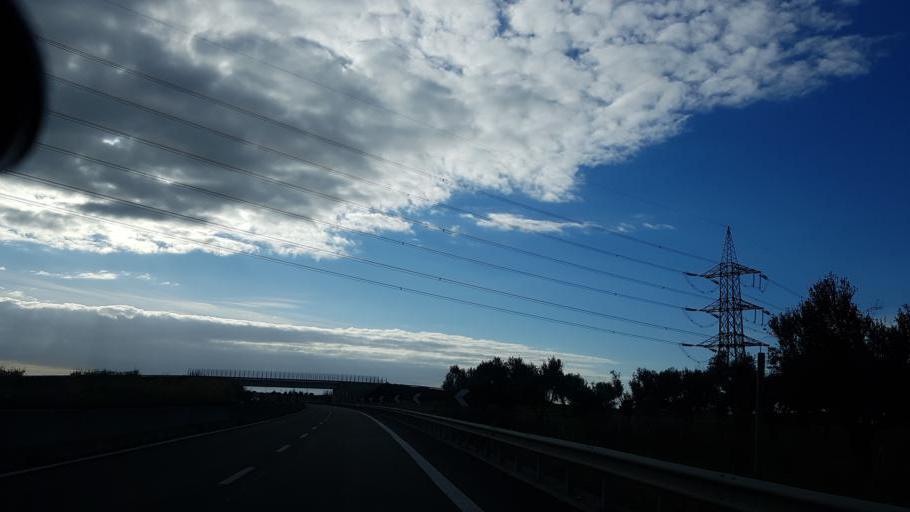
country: IT
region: Apulia
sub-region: Provincia di Brindisi
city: La Rosa
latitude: 40.6020
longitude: 17.9656
